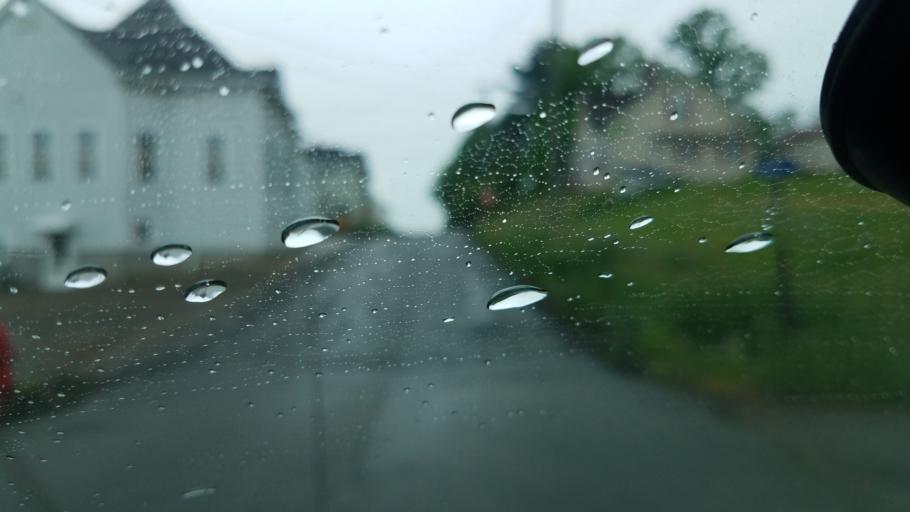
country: US
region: Ohio
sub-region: Jefferson County
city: Wintersville
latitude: 40.2722
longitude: -80.7793
